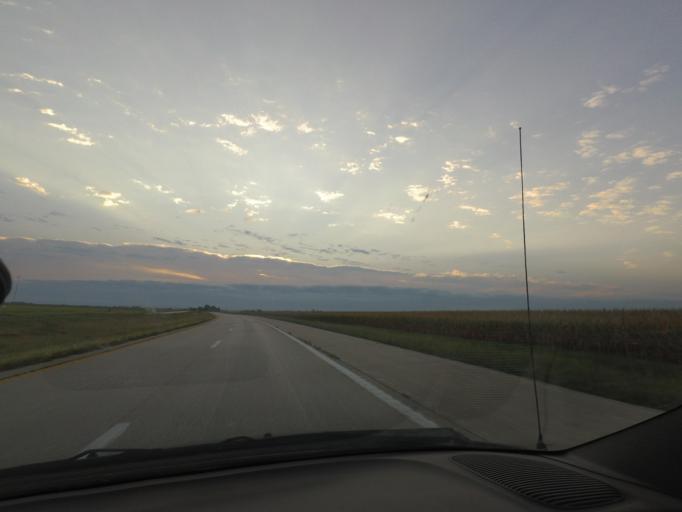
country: US
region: Missouri
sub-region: Macon County
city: Macon
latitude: 39.7497
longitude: -92.2985
